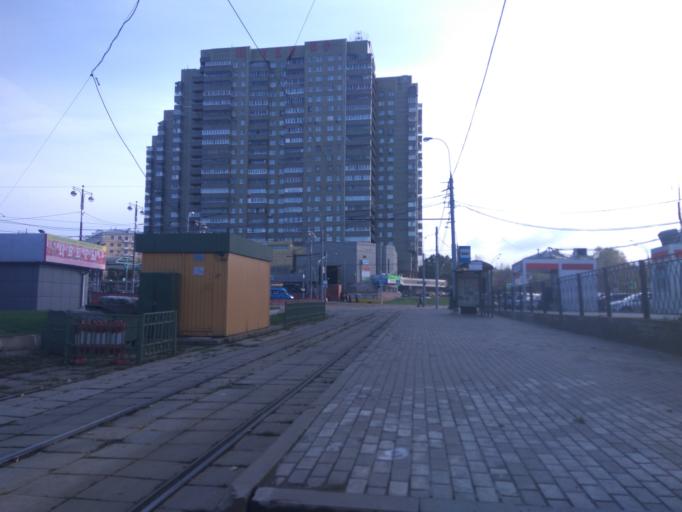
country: RU
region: Moscow
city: Pokrovskoye-Streshnevo
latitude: 55.8103
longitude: 37.4613
